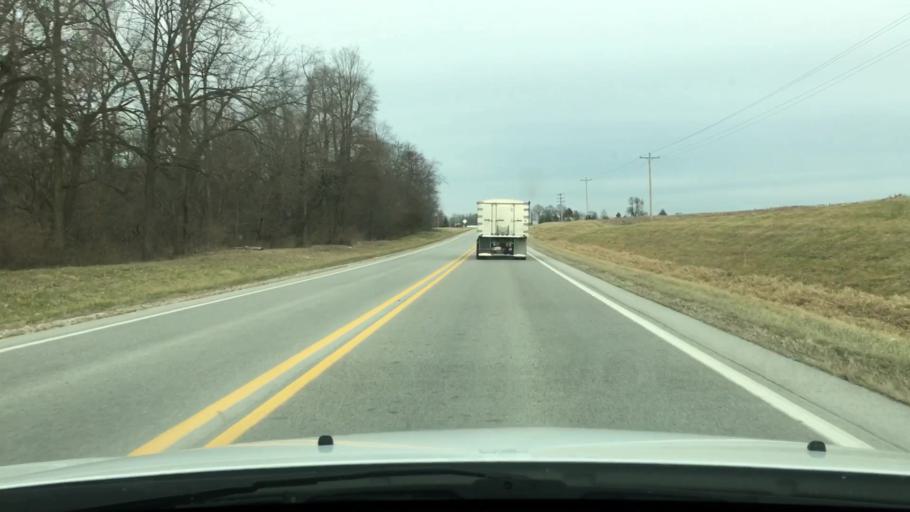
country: US
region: Illinois
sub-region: Pike County
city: Pittsfield
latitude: 39.6397
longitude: -90.7866
